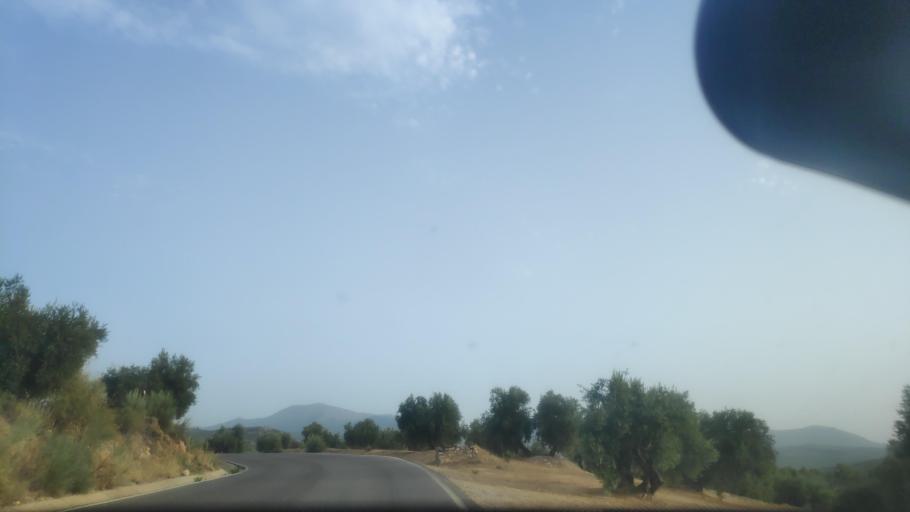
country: ES
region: Andalusia
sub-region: Provincia de Jaen
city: Jimena
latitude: 37.8366
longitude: -3.5301
